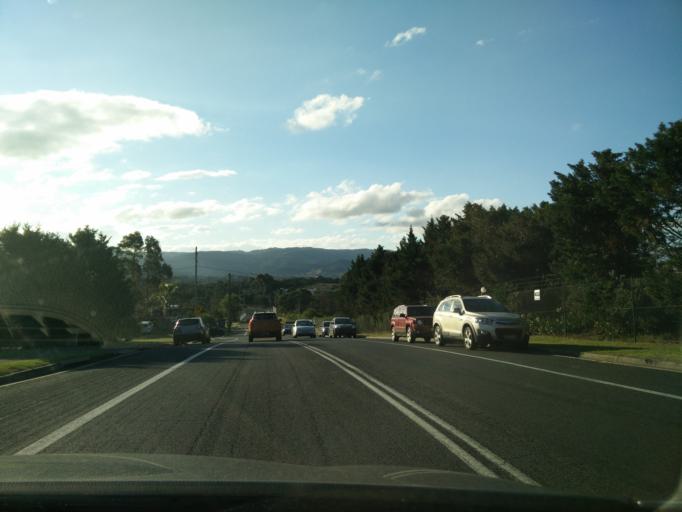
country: AU
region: New South Wales
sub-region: Wollongong
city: Berkeley
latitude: -34.4673
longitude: 150.8463
